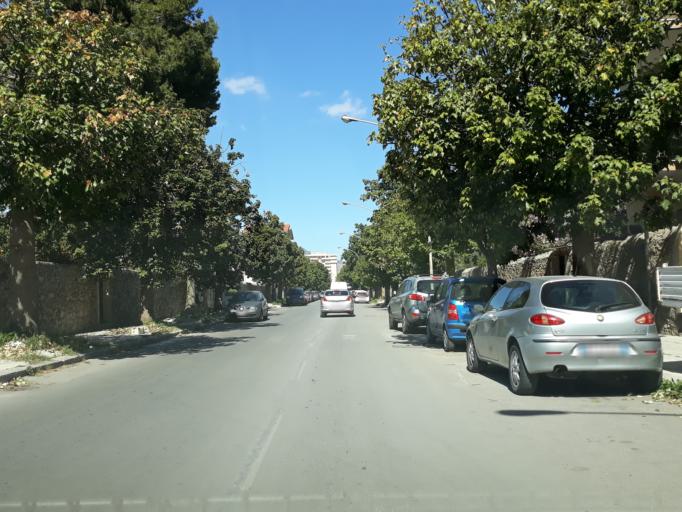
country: IT
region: Sicily
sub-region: Palermo
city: Villa Ciambra
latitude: 38.0925
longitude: 13.3204
